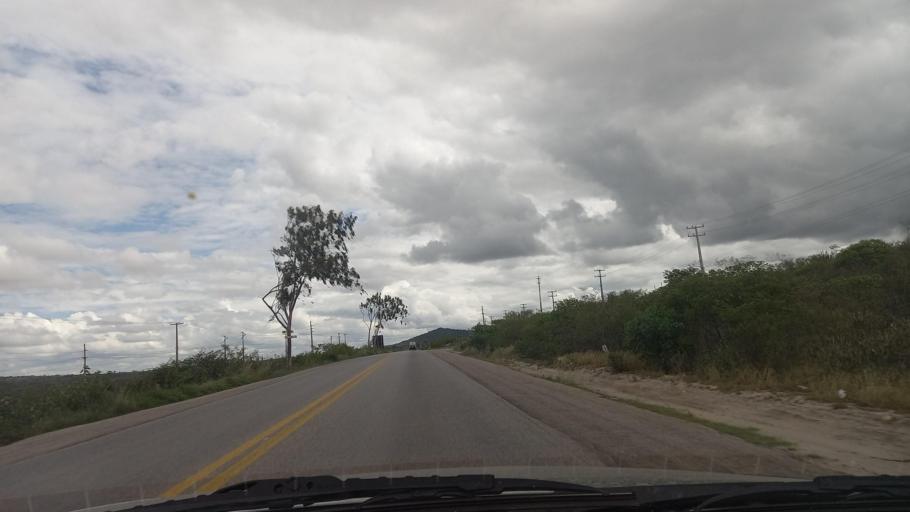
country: BR
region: Pernambuco
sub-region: Cachoeirinha
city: Cachoeirinha
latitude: -8.3334
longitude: -36.1515
